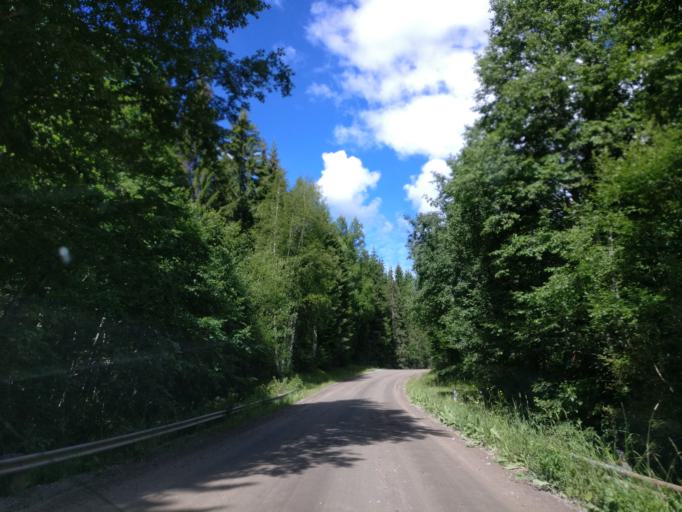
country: SE
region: Vaermland
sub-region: Hagfors Kommun
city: Ekshaerad
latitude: 60.0529
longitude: 13.4801
